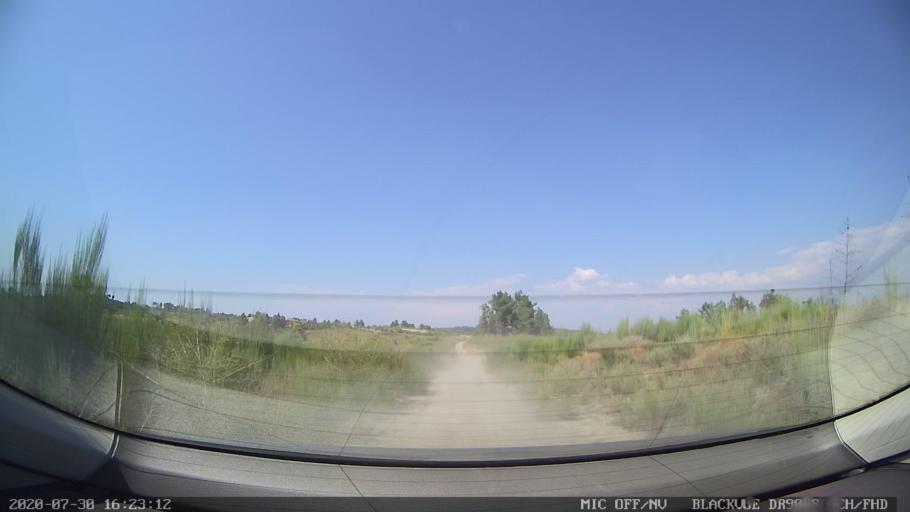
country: PT
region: Vila Real
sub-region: Murca
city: Murca
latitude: 41.3188
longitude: -7.4917
